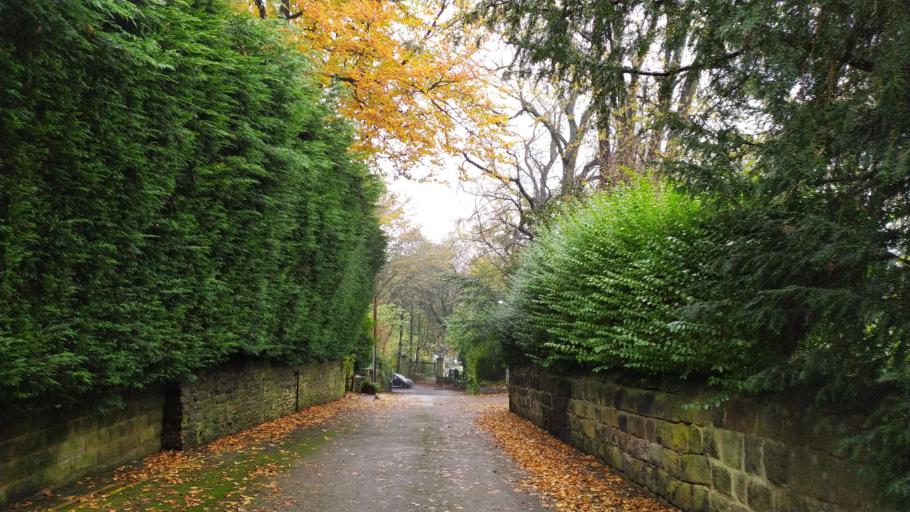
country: GB
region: England
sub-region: City and Borough of Leeds
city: Leeds
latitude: 53.8211
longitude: -1.5741
